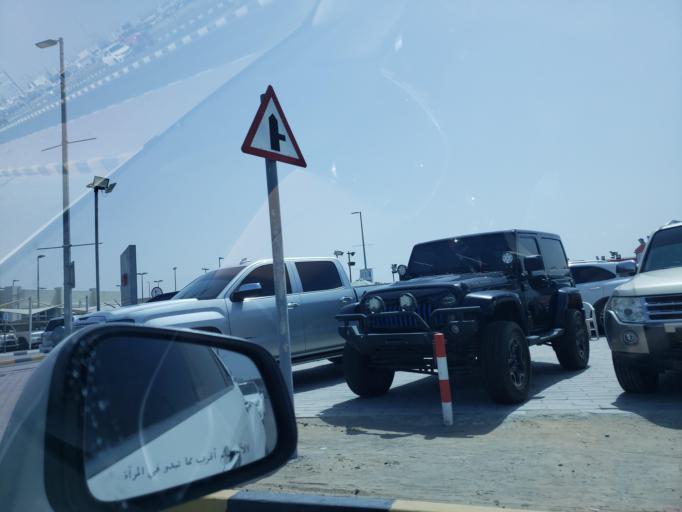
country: AE
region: Ash Shariqah
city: Sharjah
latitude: 25.3415
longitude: 55.4766
